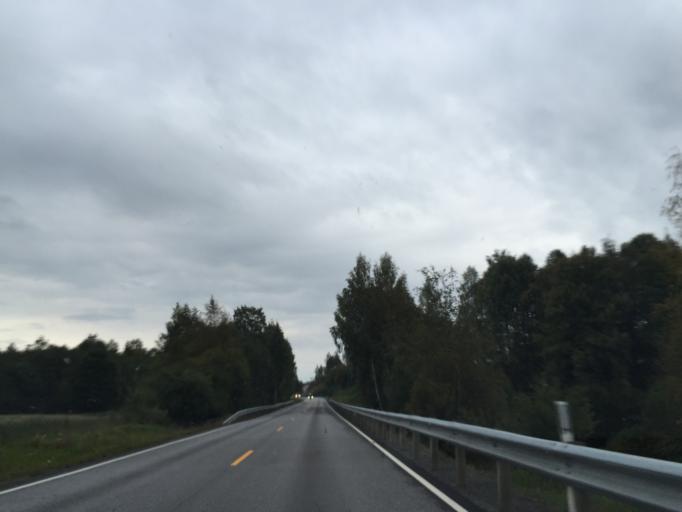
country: NO
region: Hedmark
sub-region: Nord-Odal
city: Sand
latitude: 60.3740
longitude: 11.5493
